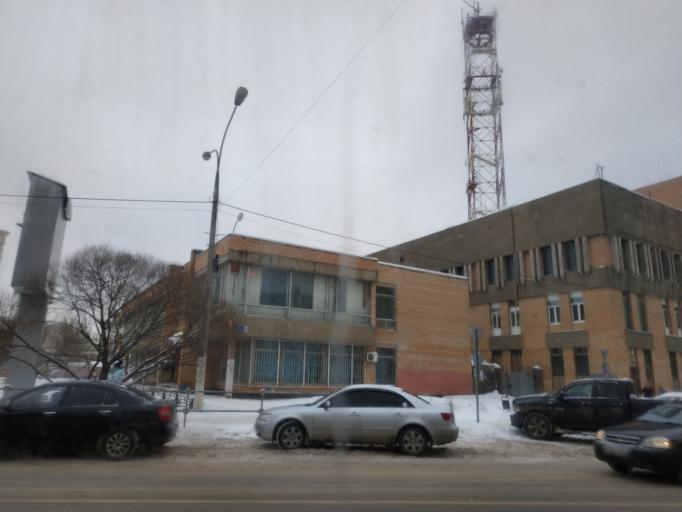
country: RU
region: Moskovskaya
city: Shchelkovo
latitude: 55.9255
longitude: 37.9936
